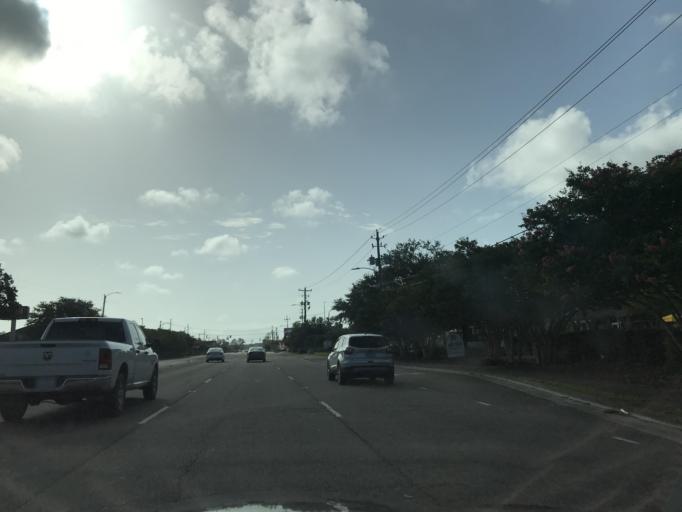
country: US
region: North Carolina
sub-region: New Hanover County
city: Wilmington
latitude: 34.2170
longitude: -77.9065
